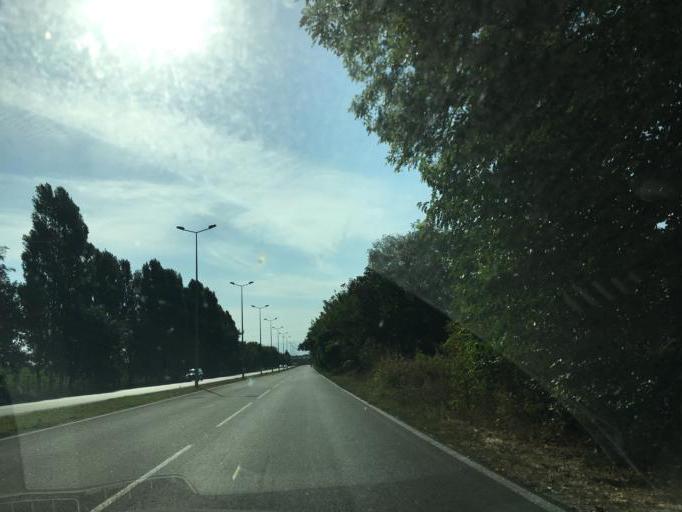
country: BG
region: Pazardzhik
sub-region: Obshtina Pazardzhik
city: Pazardzhik
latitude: 42.2165
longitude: 24.3177
